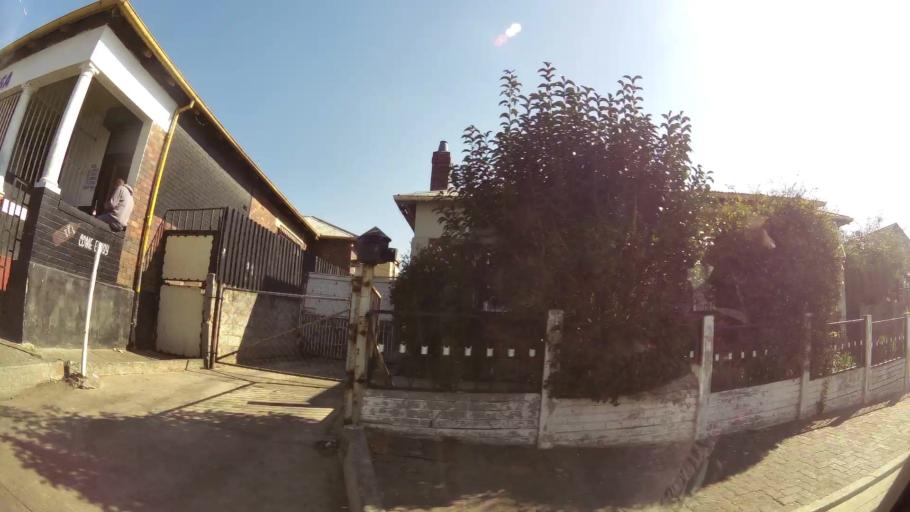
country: ZA
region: Gauteng
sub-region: City of Johannesburg Metropolitan Municipality
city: Johannesburg
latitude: -26.2538
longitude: 28.0551
